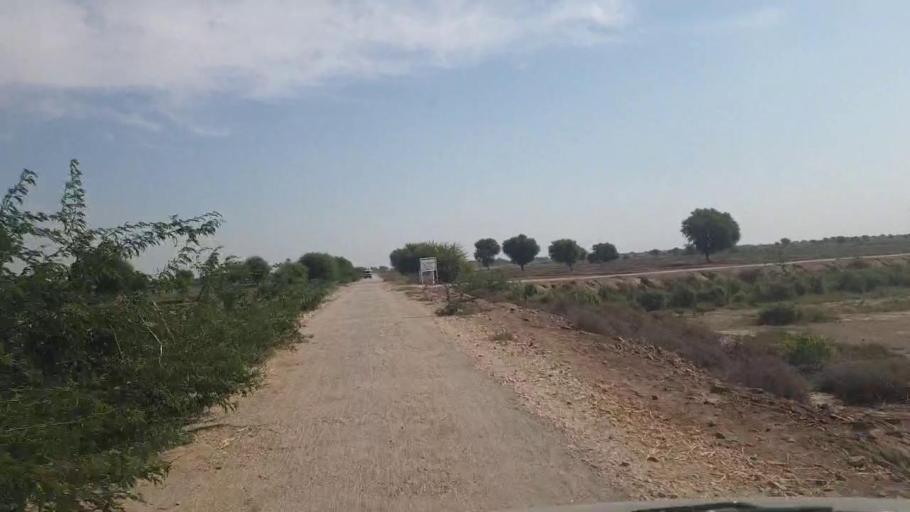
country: PK
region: Sindh
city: Tando Bago
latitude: 24.9439
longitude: 69.0918
